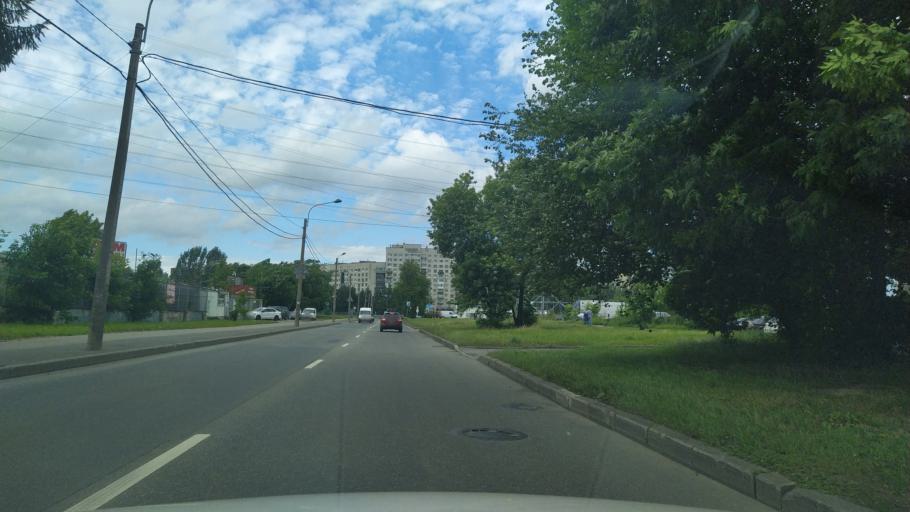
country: RU
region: Leningrad
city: Finlyandskiy
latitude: 59.9768
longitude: 30.3831
